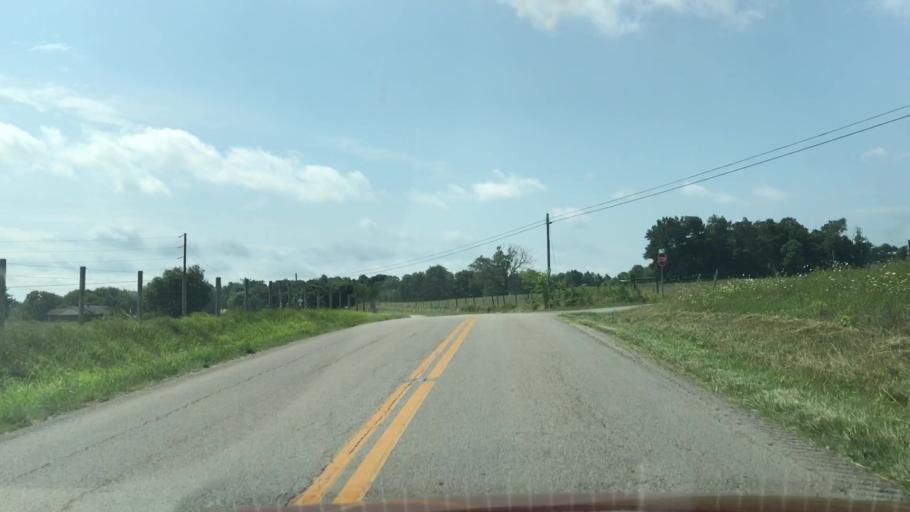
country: US
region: Kentucky
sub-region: Barren County
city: Glasgow
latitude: 36.9066
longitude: -85.8683
